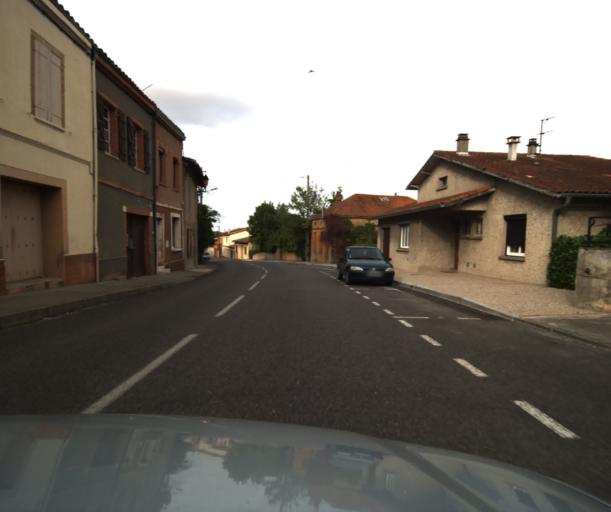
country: FR
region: Midi-Pyrenees
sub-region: Departement du Tarn-et-Garonne
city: Beaumont-de-Lomagne
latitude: 43.8835
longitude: 0.9926
